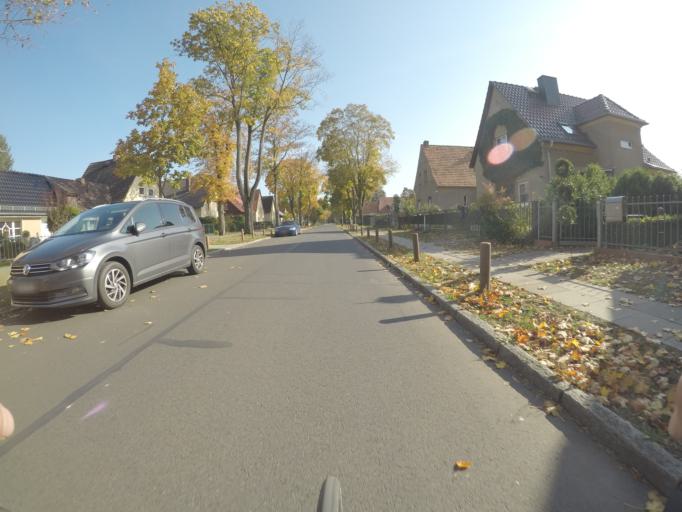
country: DE
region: Brandenburg
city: Hohen Neuendorf
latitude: 52.6787
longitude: 13.2532
